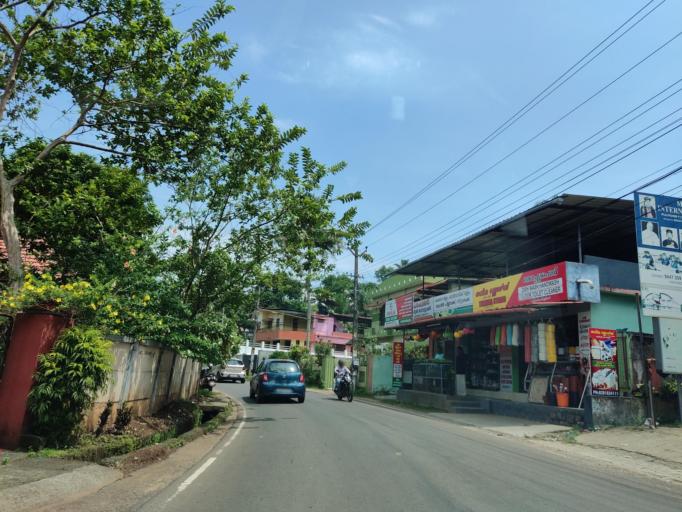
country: IN
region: Kerala
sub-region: Alappuzha
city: Chengannur
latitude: 9.3069
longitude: 76.5883
